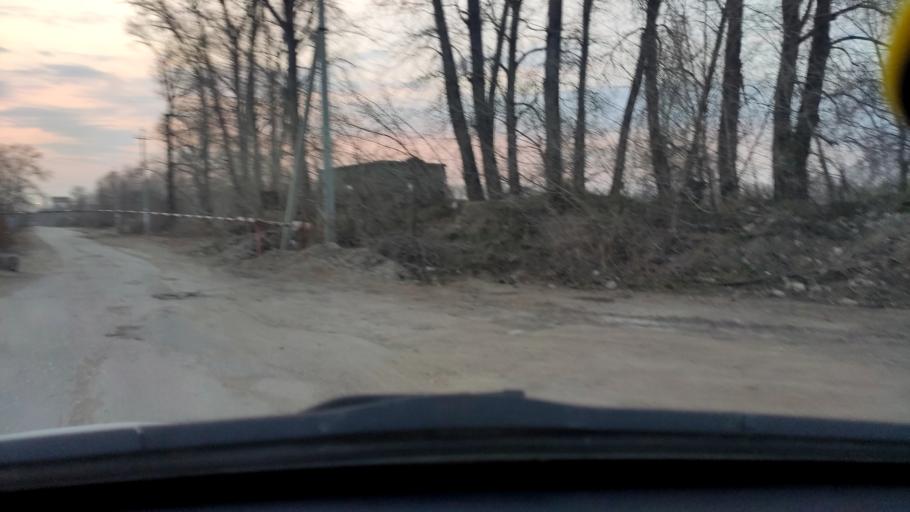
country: RU
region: Samara
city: Zhigulevsk
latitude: 53.4569
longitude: 49.5176
